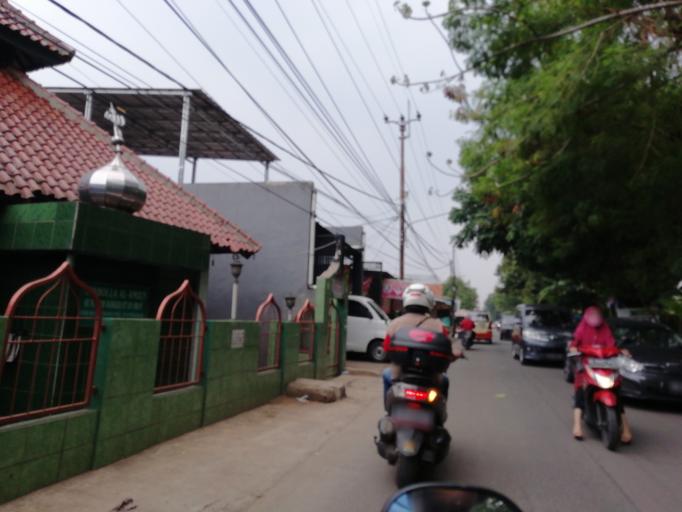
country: ID
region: West Java
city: Cibinong
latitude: -6.4737
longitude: 106.8032
